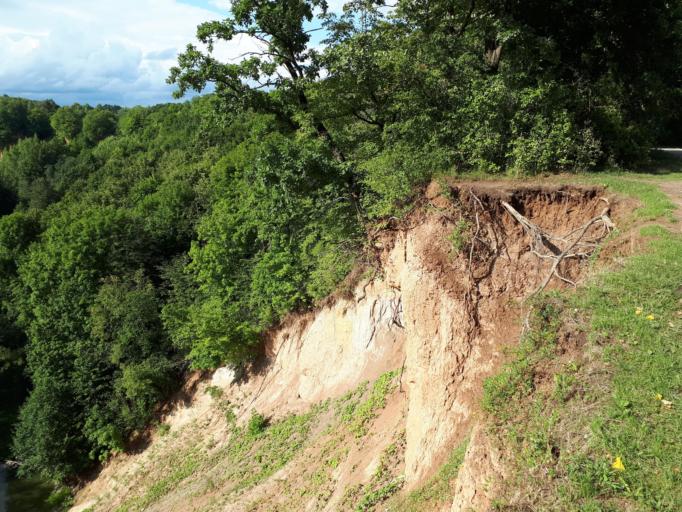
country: LT
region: Kauno apskritis
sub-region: Kaunas
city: Aleksotas
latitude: 54.8400
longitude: 23.9117
